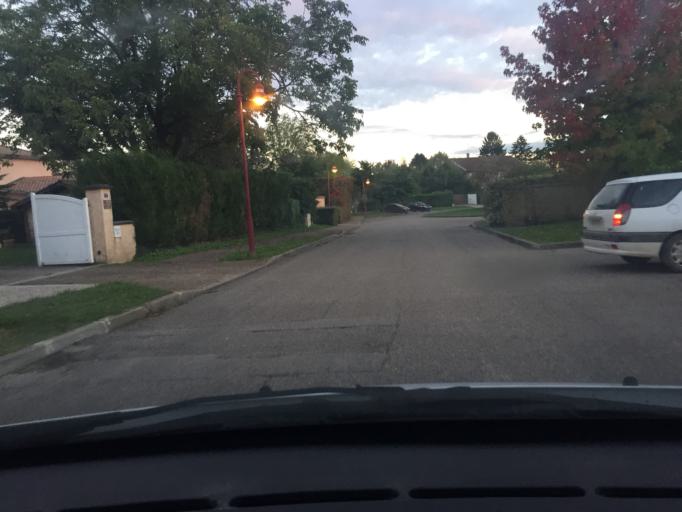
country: FR
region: Rhone-Alpes
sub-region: Departement de l'Ain
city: Saint-Maurice-de-Beynost
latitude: 45.8360
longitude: 4.9826
